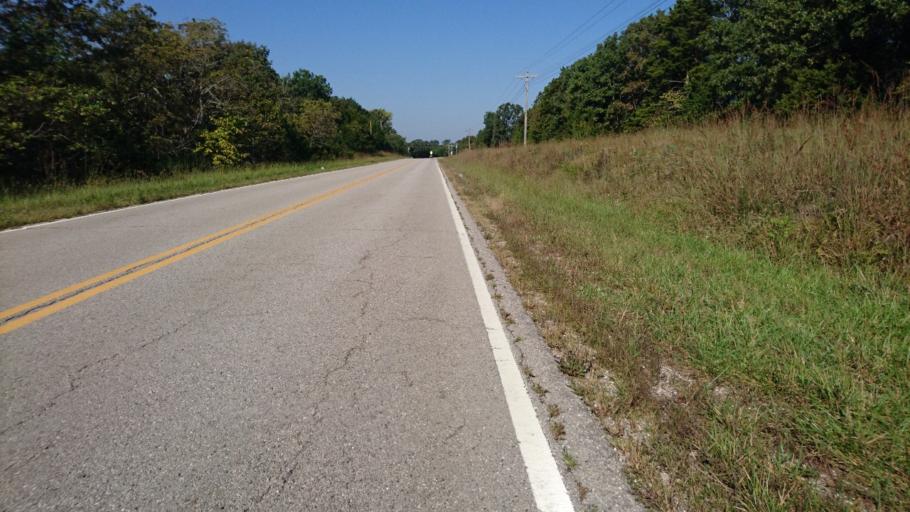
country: US
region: Missouri
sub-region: Pulaski County
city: Richland
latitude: 37.7513
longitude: -92.3654
